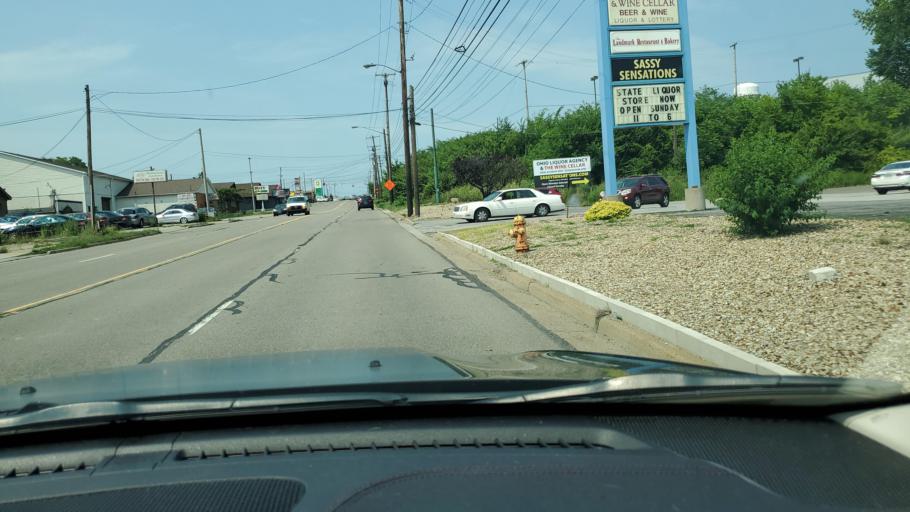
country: US
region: Ohio
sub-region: Mahoning County
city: Austintown
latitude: 41.1006
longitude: -80.7110
